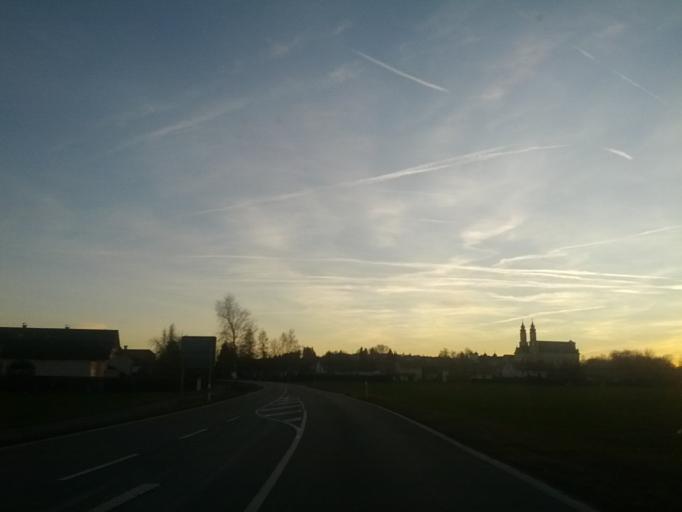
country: DE
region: Baden-Wuerttemberg
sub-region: Tuebingen Region
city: Rot an der Rot
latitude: 48.0201
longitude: 10.0361
